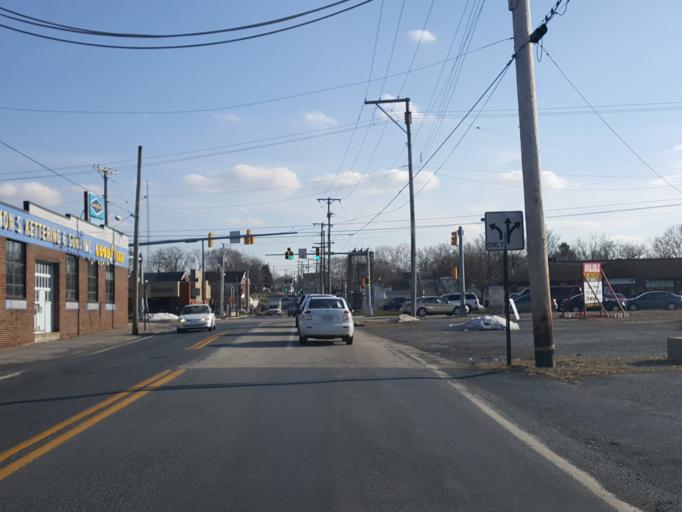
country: US
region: Pennsylvania
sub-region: Lebanon County
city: Pleasant Hill
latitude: 40.3390
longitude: -76.4397
